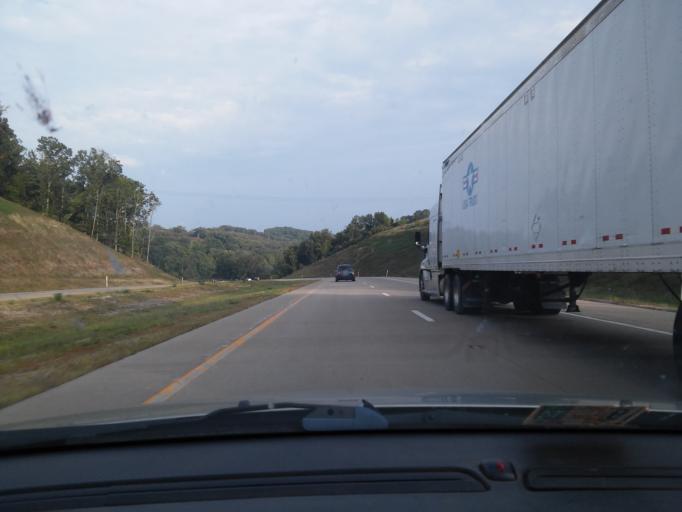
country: US
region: West Virginia
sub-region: Mason County
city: Point Pleasant
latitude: 38.7724
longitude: -82.0554
